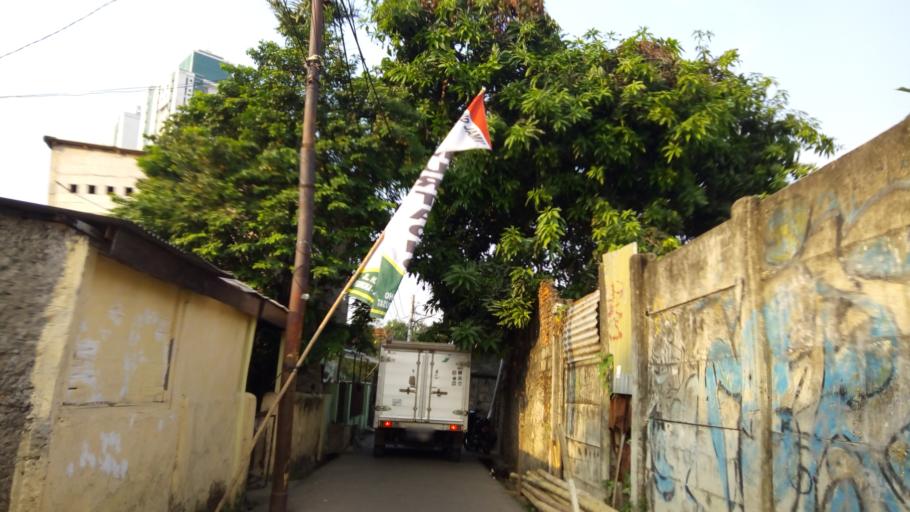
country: ID
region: Jakarta Raya
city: Jakarta
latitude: -6.1972
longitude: 106.8546
